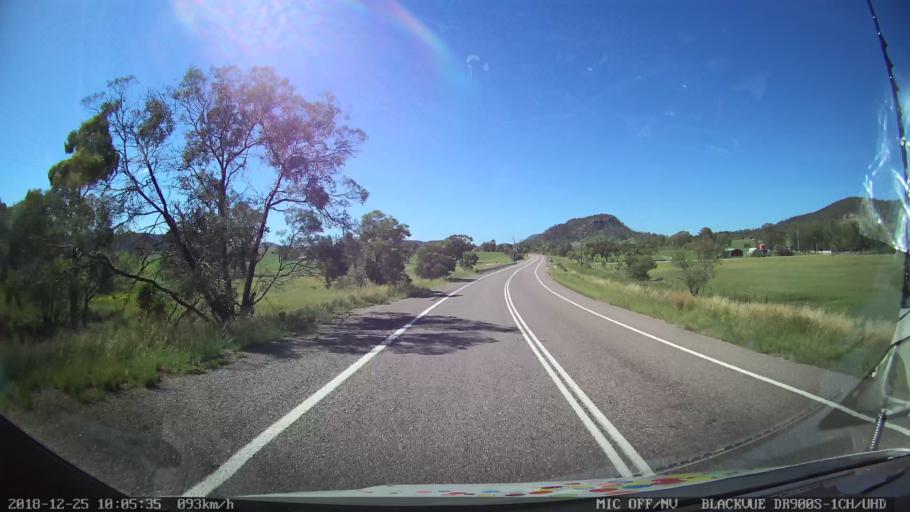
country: AU
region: New South Wales
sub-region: Upper Hunter Shire
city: Merriwa
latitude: -32.2490
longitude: 150.4867
